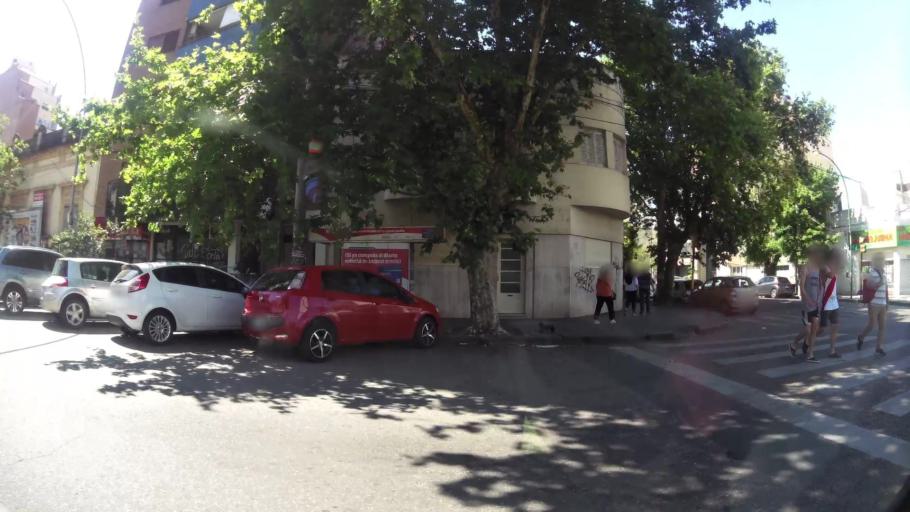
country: AR
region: Cordoba
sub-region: Departamento de Capital
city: Cordoba
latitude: -31.4144
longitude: -64.1685
